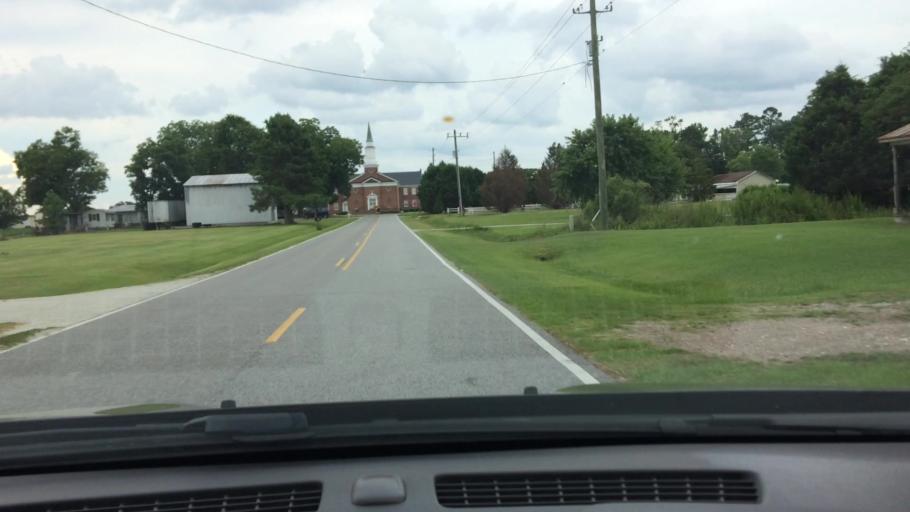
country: US
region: North Carolina
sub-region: Pitt County
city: Ayden
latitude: 35.4313
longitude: -77.4127
